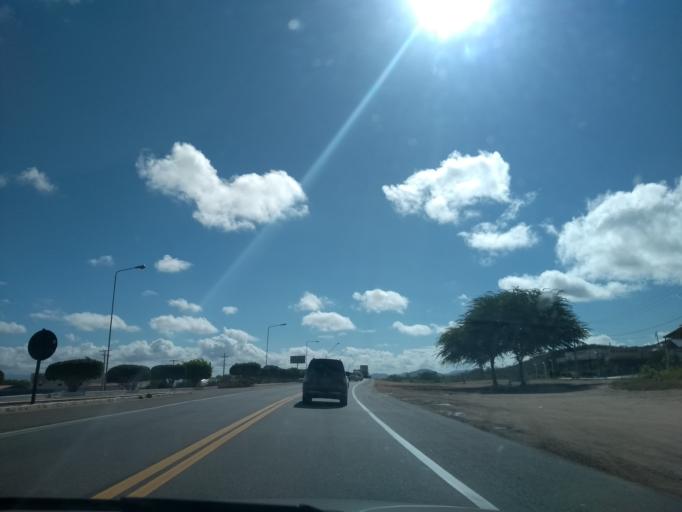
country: BR
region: Bahia
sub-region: Amargosa
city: Amargosa
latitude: -12.8665
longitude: -39.8550
